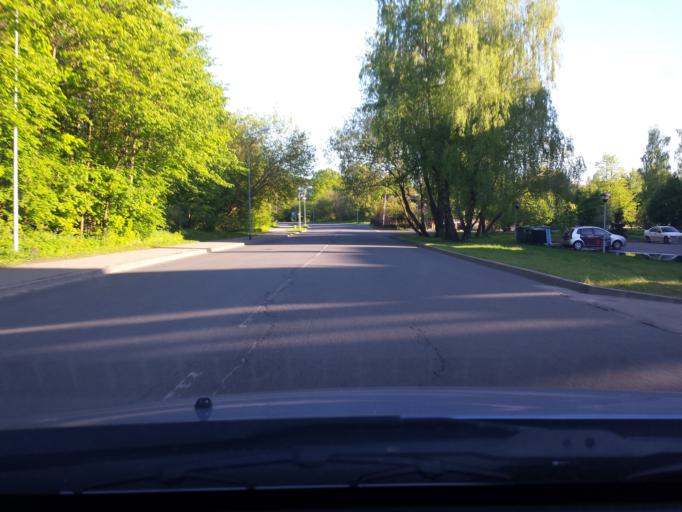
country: LV
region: Riga
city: Jaunciems
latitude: 56.9967
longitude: 24.1715
